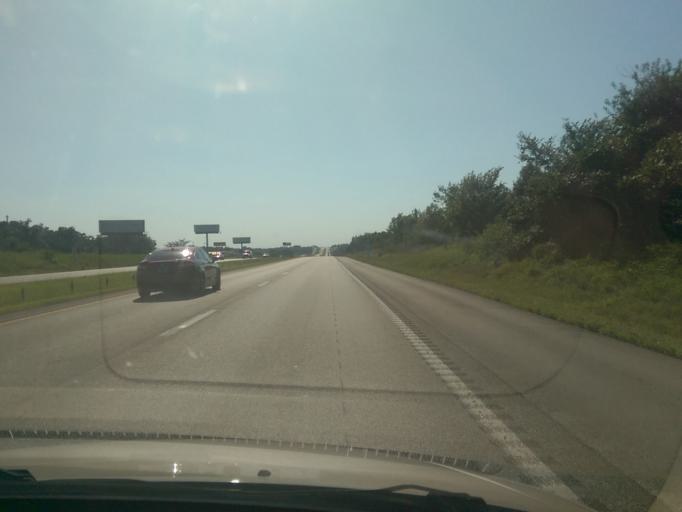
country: US
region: Missouri
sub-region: Saline County
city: Sweet Springs
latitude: 38.9726
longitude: -93.2981
